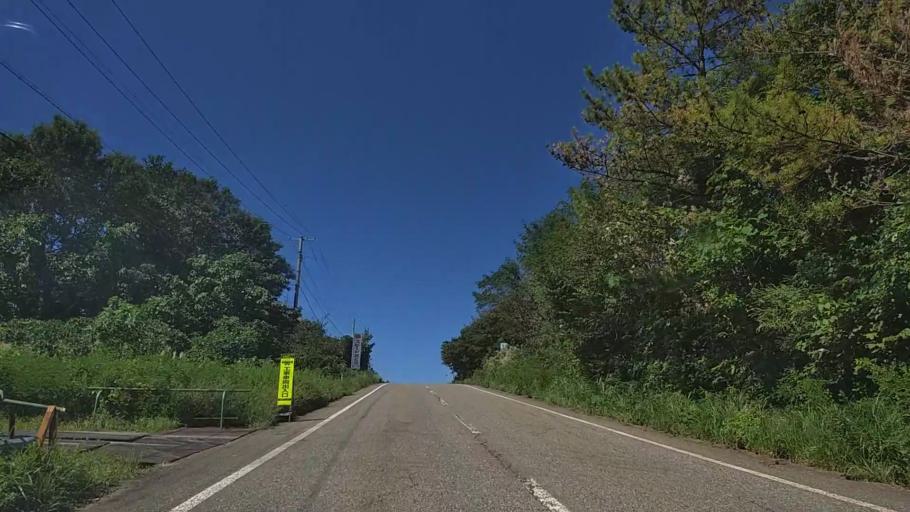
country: JP
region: Niigata
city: Joetsu
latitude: 37.1699
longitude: 138.1075
